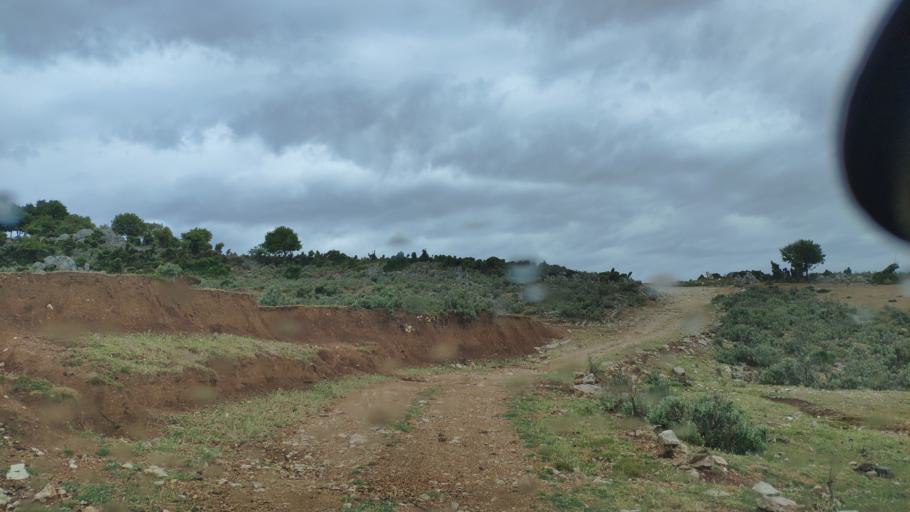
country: GR
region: West Greece
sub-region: Nomos Aitolias kai Akarnanias
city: Archontochorion
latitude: 38.6816
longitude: 21.0211
